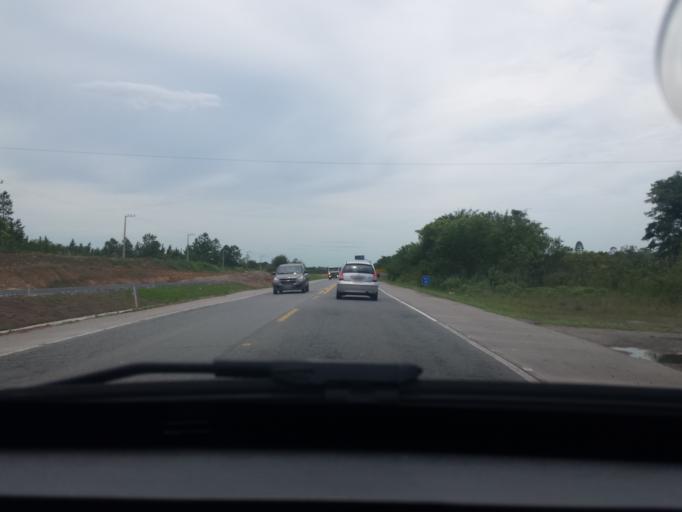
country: BR
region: Santa Catarina
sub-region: Gaspar
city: Gaspar
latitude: -26.8809
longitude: -48.8459
